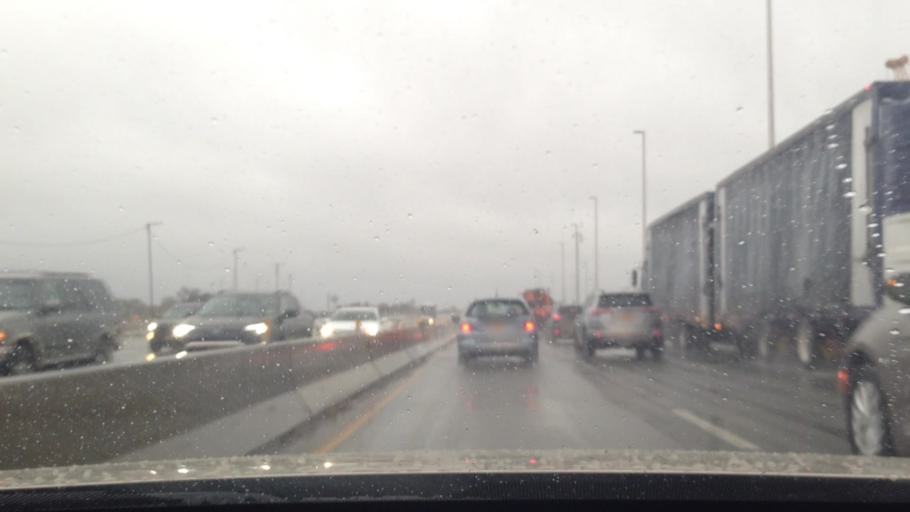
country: US
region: New York
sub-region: Queens County
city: Long Island City
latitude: 40.7313
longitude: -73.9255
